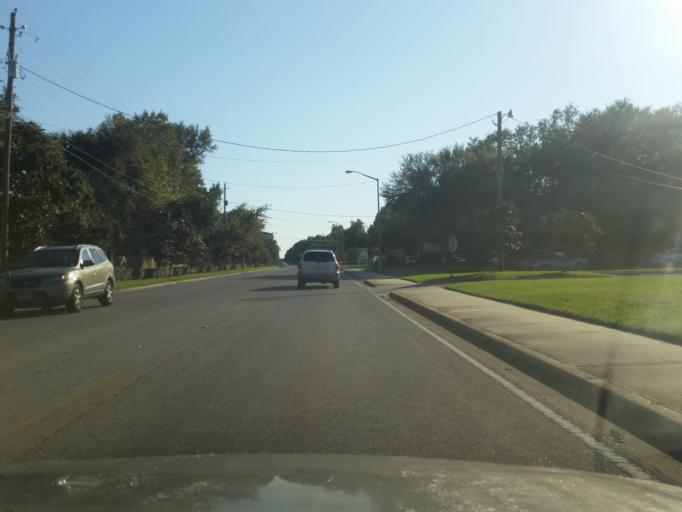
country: US
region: Florida
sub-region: Escambia County
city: East Pensacola Heights
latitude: 30.4688
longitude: -87.1749
